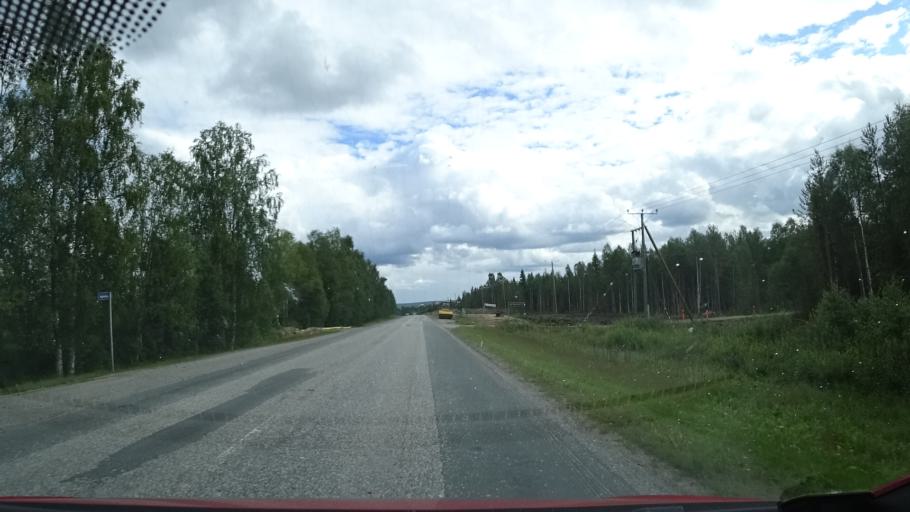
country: FI
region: Lapland
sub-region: Rovaniemi
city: Rovaniemi
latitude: 66.5436
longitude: 25.7113
